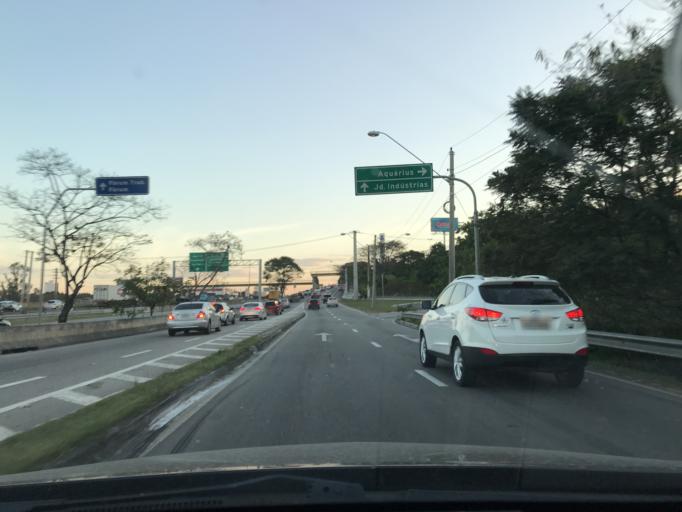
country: BR
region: Sao Paulo
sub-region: Sao Jose Dos Campos
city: Sao Jose dos Campos
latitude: -23.2218
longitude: -45.9029
